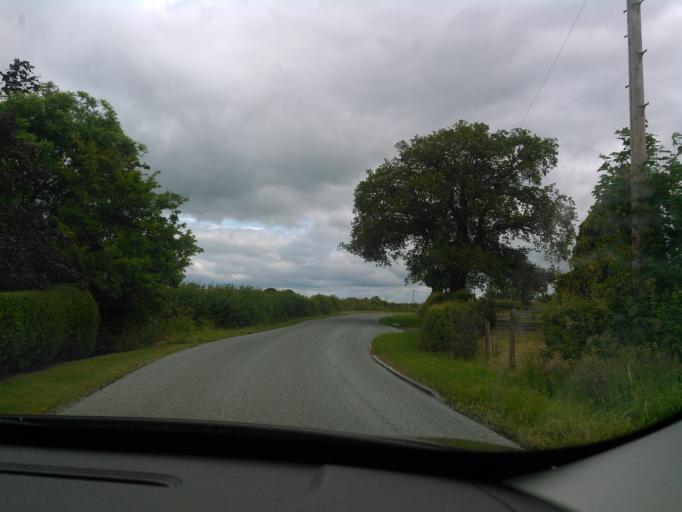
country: GB
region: England
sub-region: Shropshire
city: Wem
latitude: 52.8981
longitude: -2.7625
